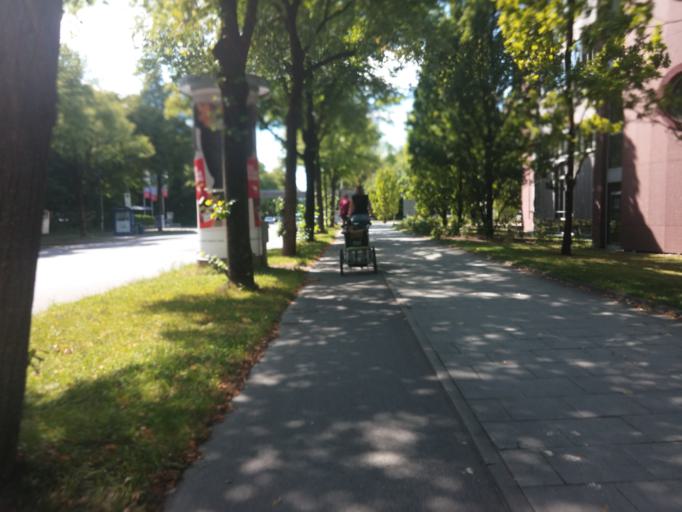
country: DE
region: Bavaria
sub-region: Upper Bavaria
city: Bogenhausen
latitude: 48.1479
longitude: 11.6267
